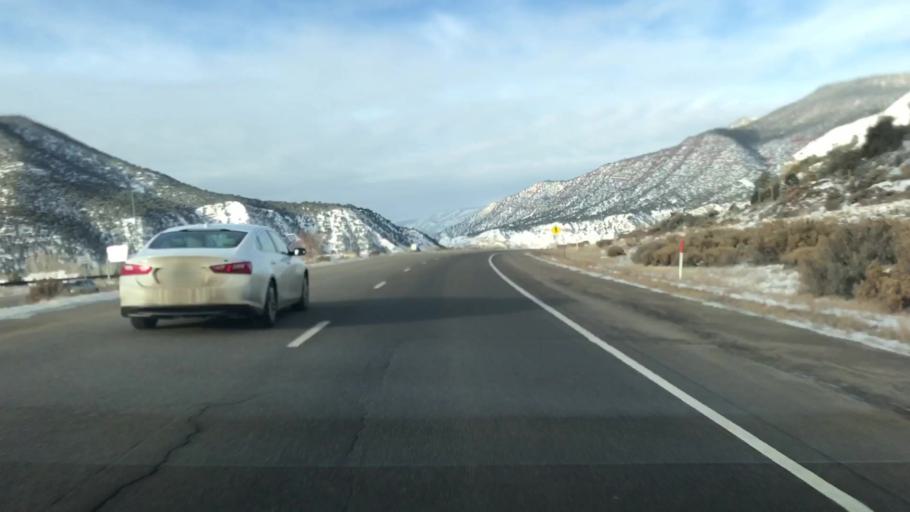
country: US
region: Colorado
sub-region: Eagle County
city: Gypsum
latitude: 39.6522
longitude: -106.9570
